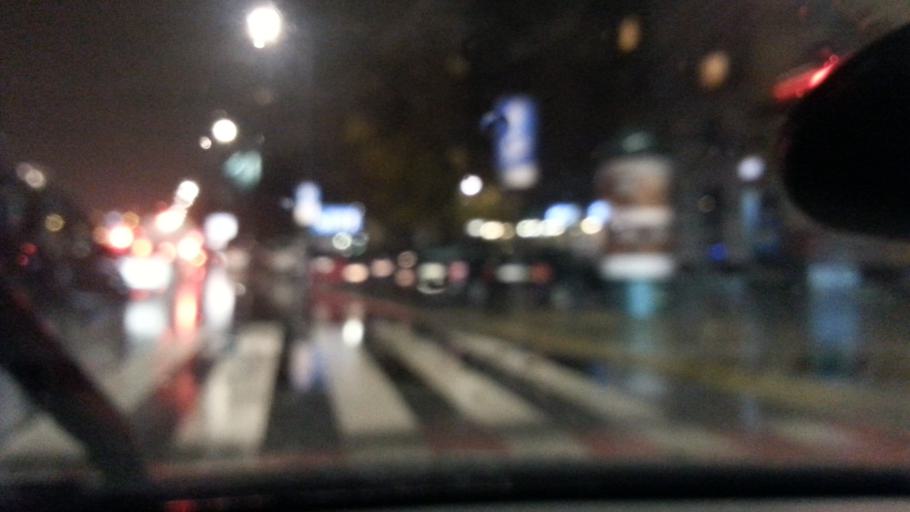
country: PL
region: Masovian Voivodeship
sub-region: Warszawa
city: Wola
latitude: 52.2396
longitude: 20.9958
